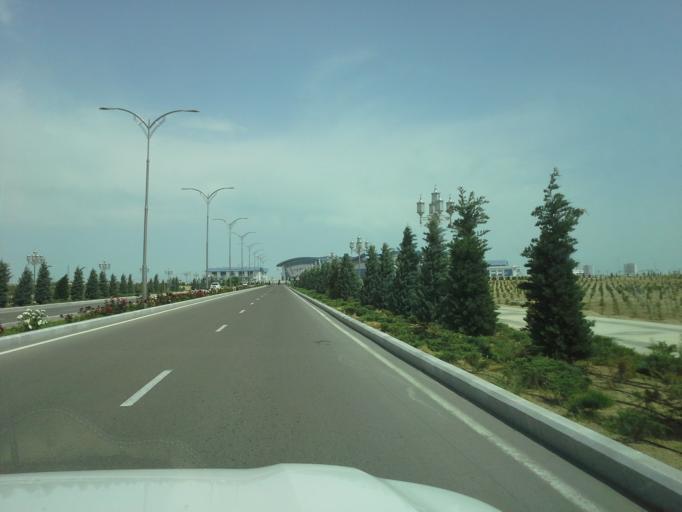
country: TM
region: Balkan
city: Turkmenbasy
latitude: 39.9676
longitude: 52.8459
